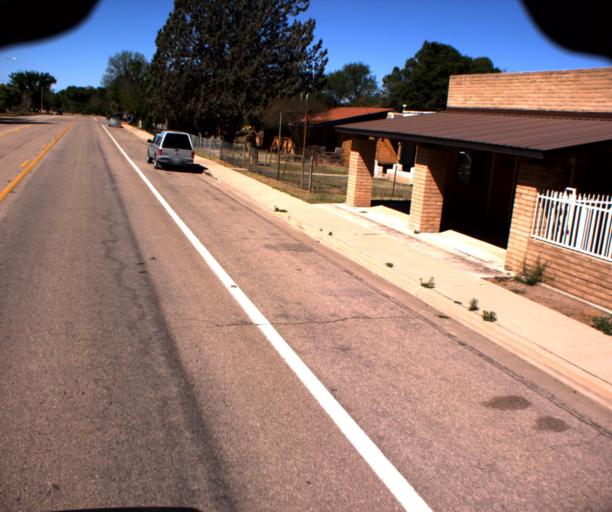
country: US
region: Arizona
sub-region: Santa Cruz County
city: Rio Rico
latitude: 31.5399
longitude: -110.7552
